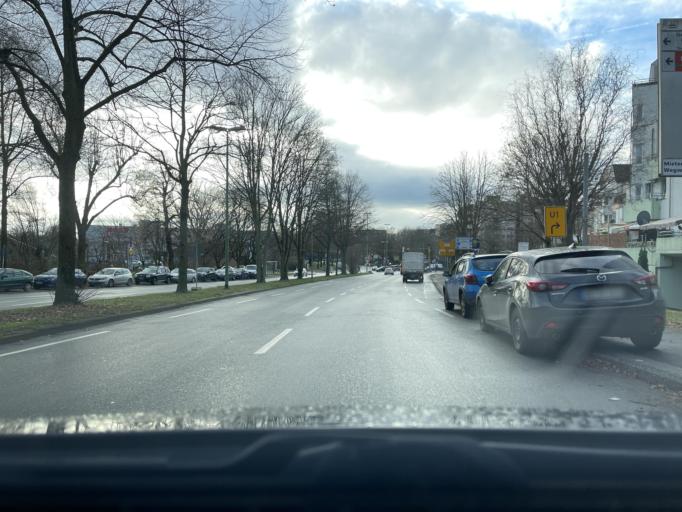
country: DE
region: North Rhine-Westphalia
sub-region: Regierungsbezirk Munster
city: Bottrop
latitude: 51.4737
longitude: 6.9562
